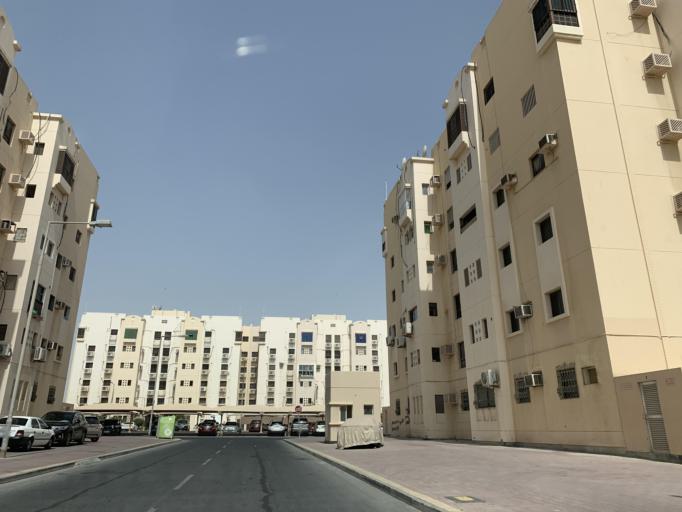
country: BH
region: Northern
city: Madinat `Isa
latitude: 26.1704
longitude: 50.5198
